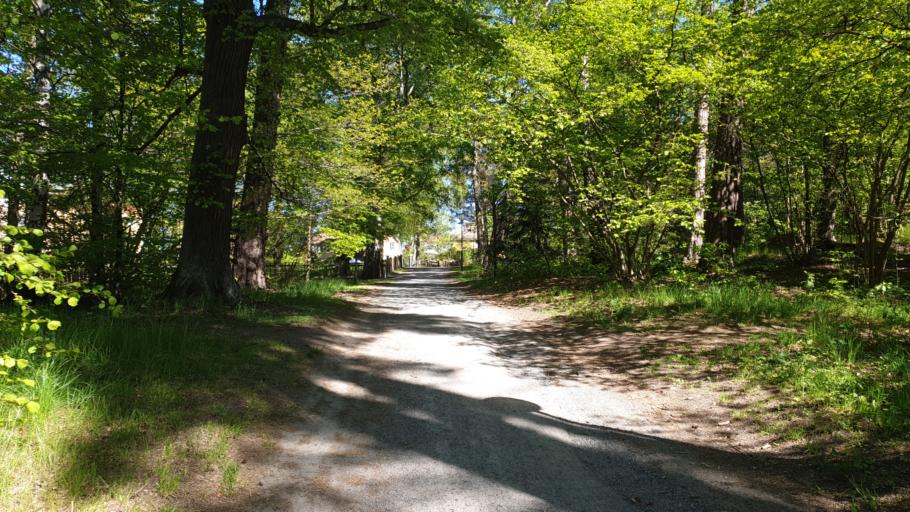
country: SE
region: Stockholm
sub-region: Norrtalje Kommun
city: Bergshamra
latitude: 59.3566
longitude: 18.0399
